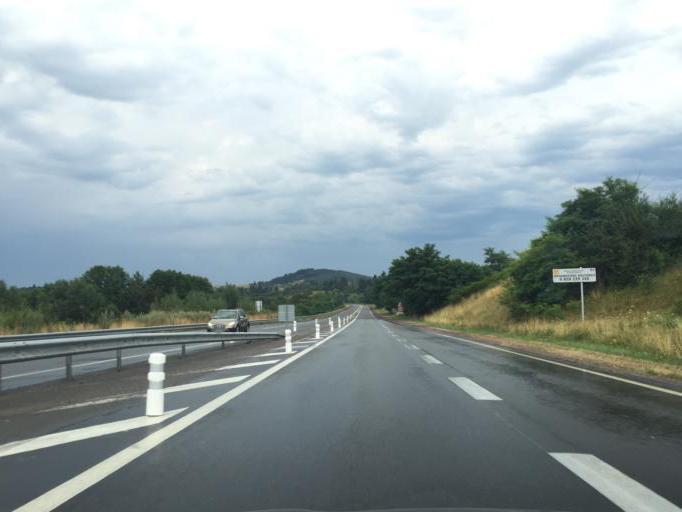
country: FR
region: Rhone-Alpes
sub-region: Departement de la Loire
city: La Pacaudiere
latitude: 46.2157
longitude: 3.7907
